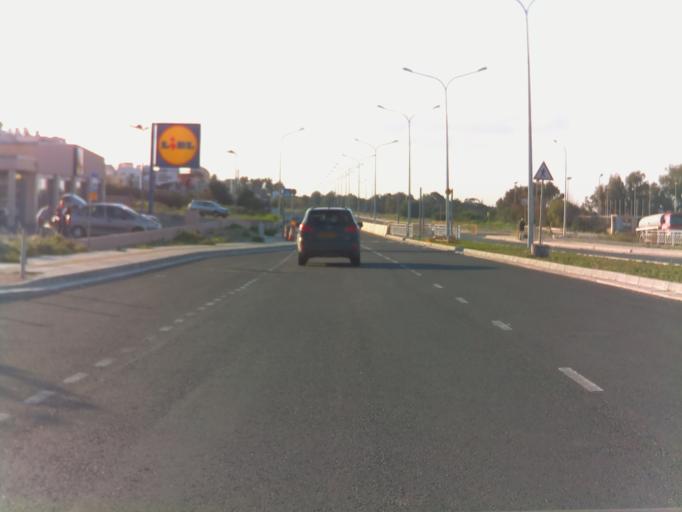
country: CY
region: Pafos
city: Chlorakas
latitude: 34.7816
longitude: 32.4059
